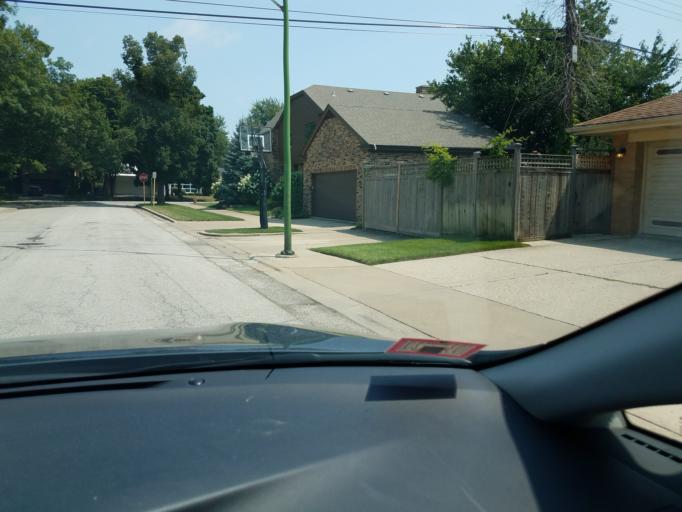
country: US
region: Illinois
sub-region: Cook County
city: Lincolnwood
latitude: 41.9956
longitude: -87.7406
